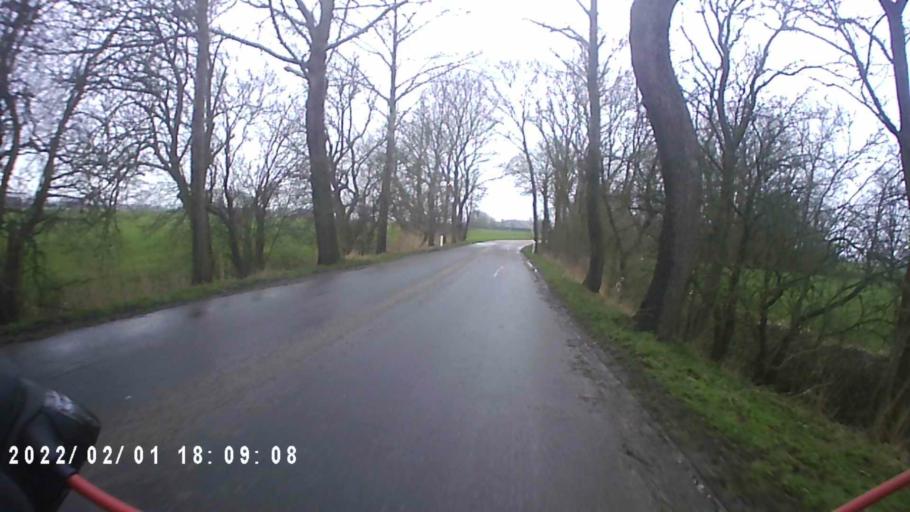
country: NL
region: Groningen
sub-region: Gemeente De Marne
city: Ulrum
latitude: 53.3434
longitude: 6.3560
